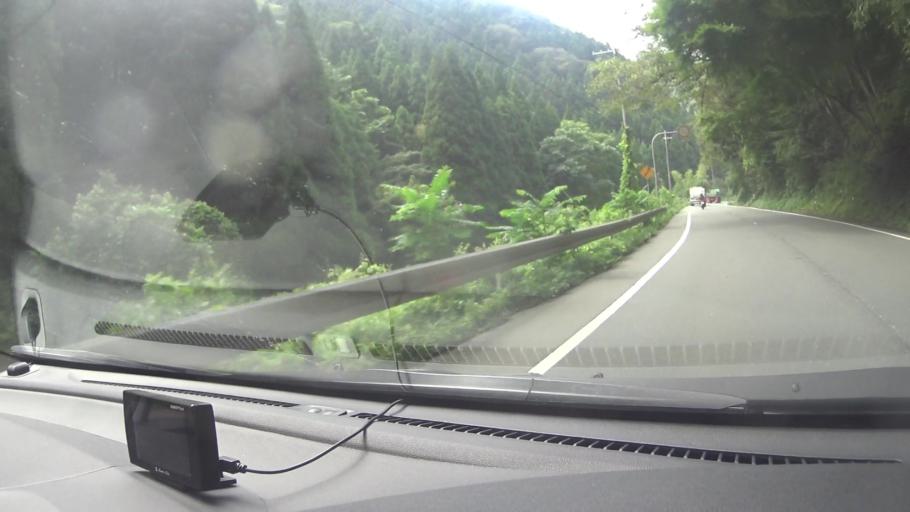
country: JP
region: Kyoto
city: Ayabe
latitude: 35.2424
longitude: 135.3063
